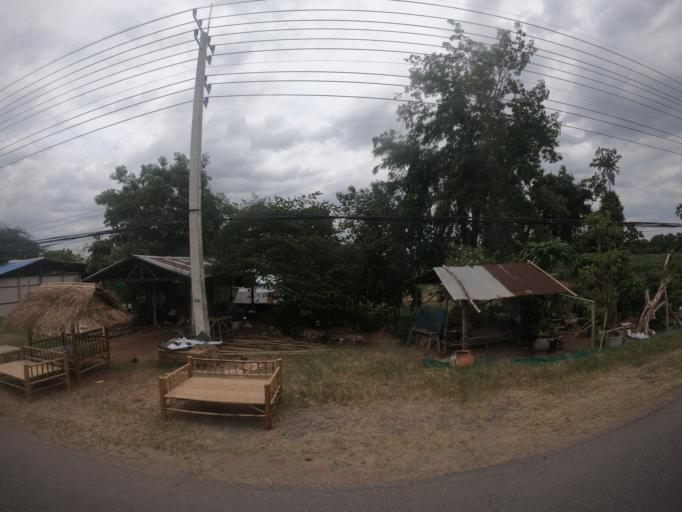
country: TH
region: Nakhon Ratchasima
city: Chok Chai
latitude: 14.8237
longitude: 102.1805
